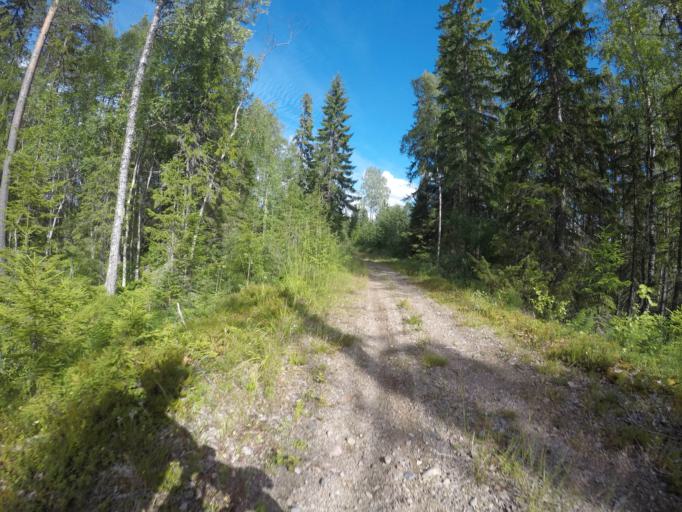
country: SE
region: OErebro
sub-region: Hallefors Kommun
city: Haellefors
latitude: 60.0137
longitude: 14.5914
